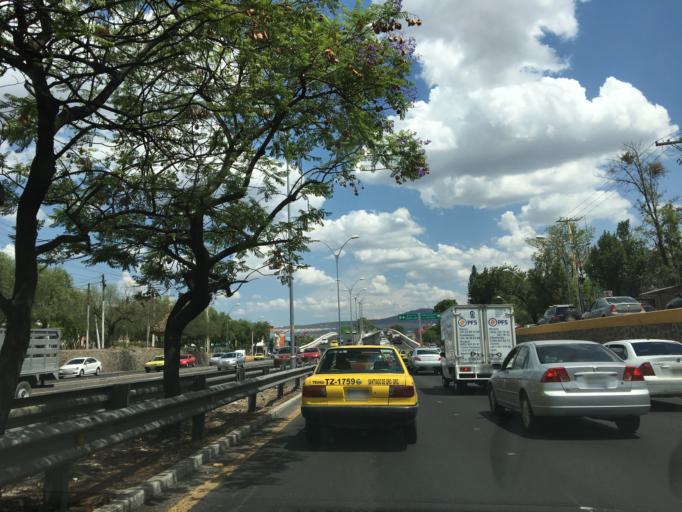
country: MX
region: Queretaro
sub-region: Queretaro
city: Santiago de Queretaro
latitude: 20.6032
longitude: -100.3769
